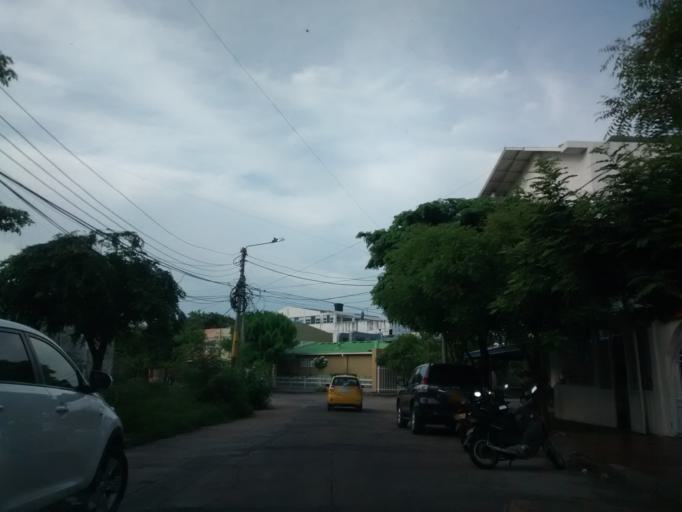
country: CO
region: Cundinamarca
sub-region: Girardot
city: Girardot City
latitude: 4.2973
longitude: -74.8018
